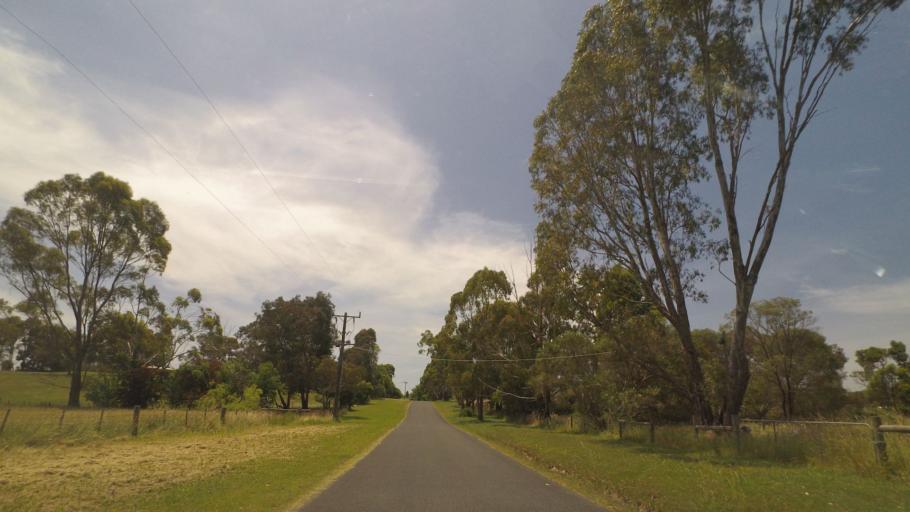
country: AU
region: Victoria
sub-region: Yarra Ranges
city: Chirnside Park
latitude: -37.7508
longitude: 145.2951
